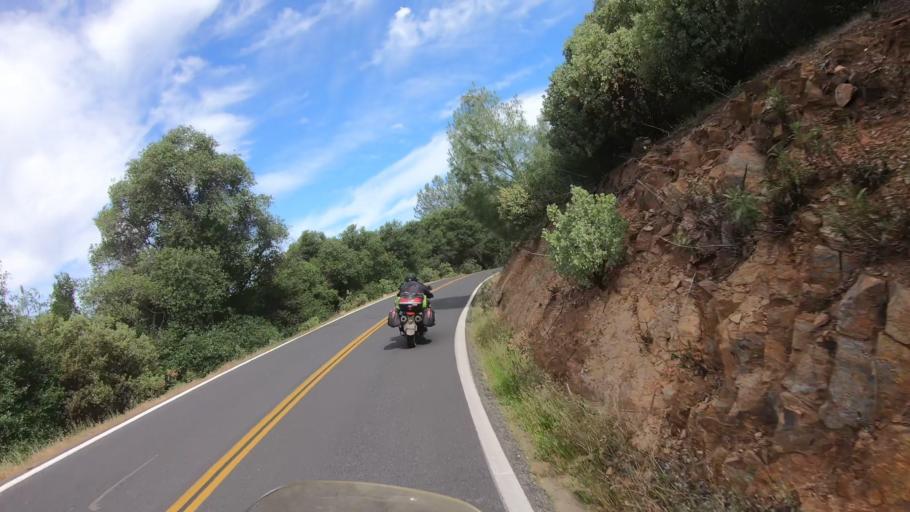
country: US
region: California
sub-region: Tuolumne County
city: Tuolumne City
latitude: 37.8550
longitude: -120.1701
